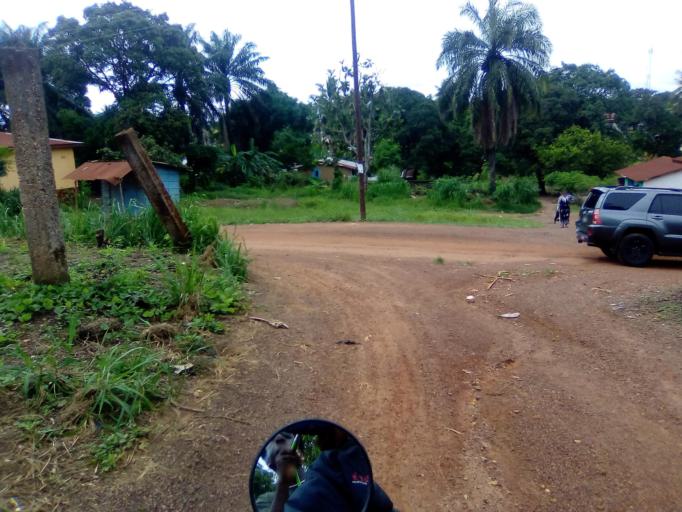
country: SL
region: Southern Province
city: Bo
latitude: 7.9422
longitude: -11.7328
